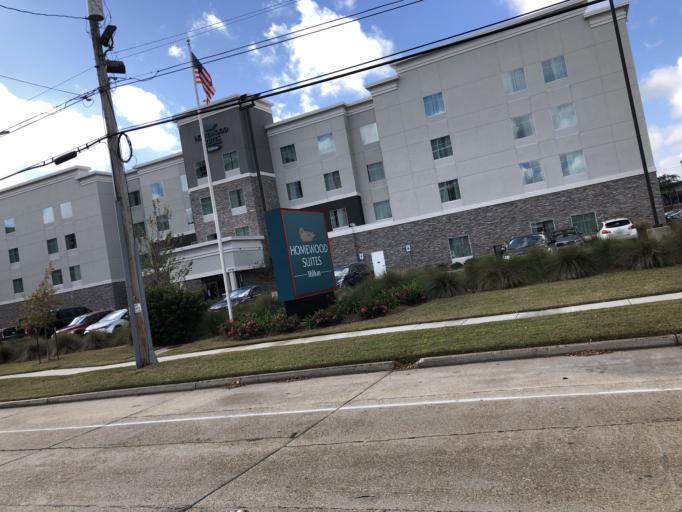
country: US
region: Louisiana
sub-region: Jefferson Parish
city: Metairie
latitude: 30.0012
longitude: -90.1596
